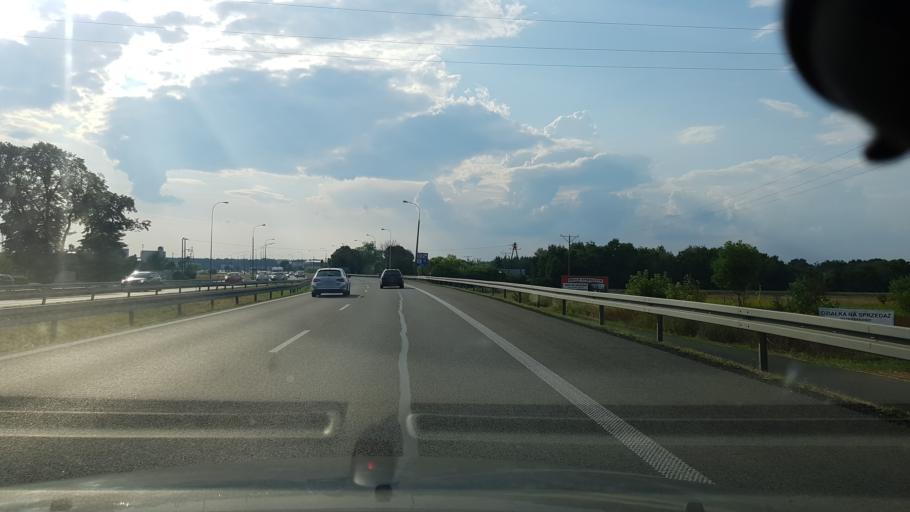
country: PL
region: Masovian Voivodeship
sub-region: Powiat nowodworski
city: Nowy Dwor Mazowiecki
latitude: 52.3864
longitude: 20.7459
